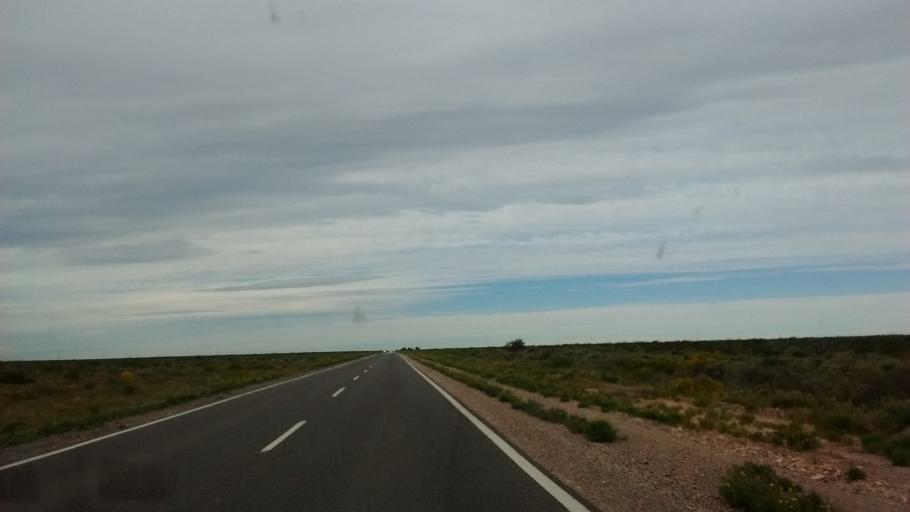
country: AR
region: Rio Negro
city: Contraalmirante Cordero
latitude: -38.3705
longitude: -68.0206
